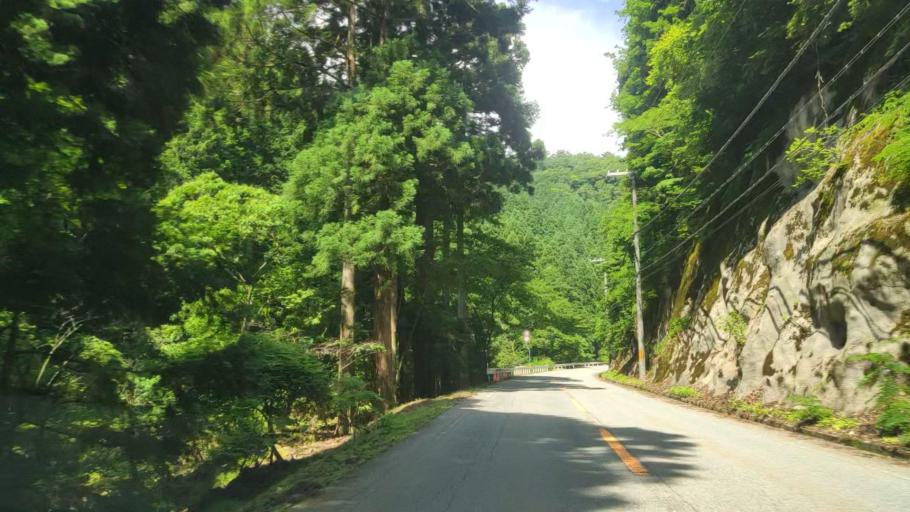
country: JP
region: Hyogo
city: Toyooka
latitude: 35.6313
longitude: 134.7838
